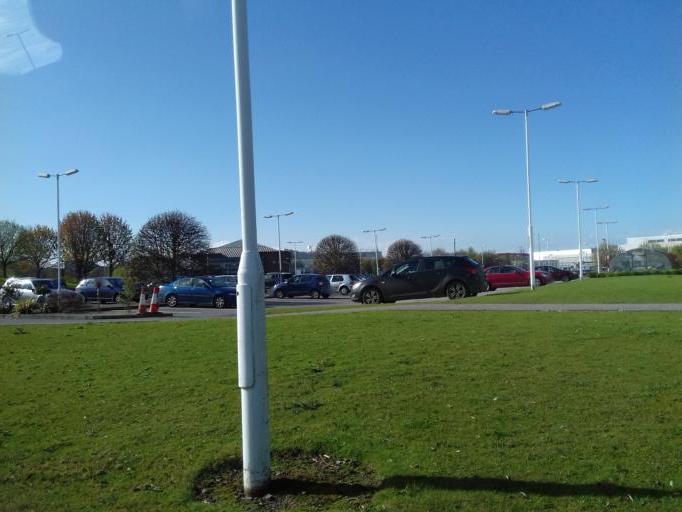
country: IE
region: Leinster
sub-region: Fingal County
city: Blanchardstown
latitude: 53.4063
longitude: -6.3537
